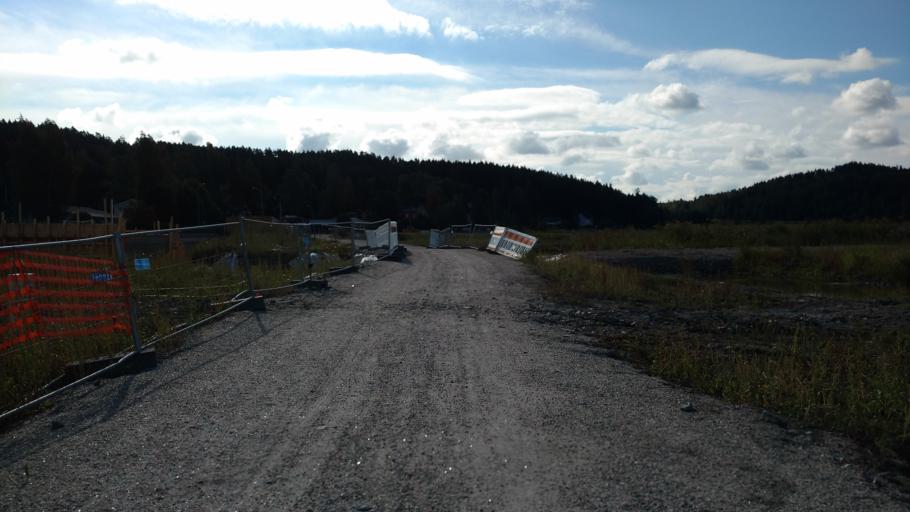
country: FI
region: Varsinais-Suomi
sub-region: Salo
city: Salo
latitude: 60.3737
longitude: 23.1682
